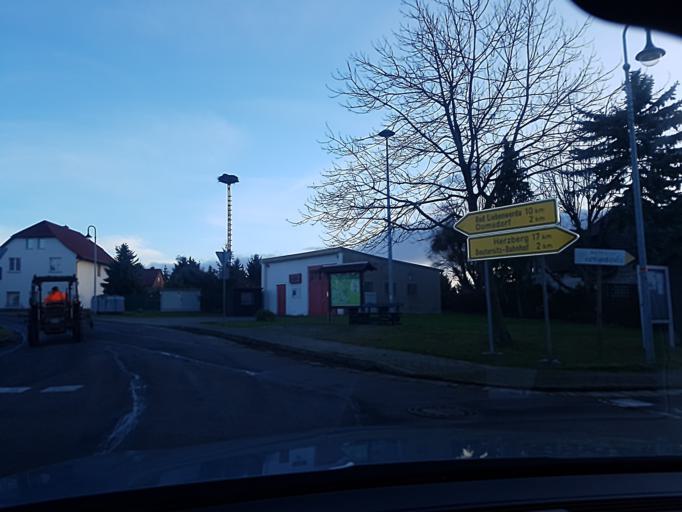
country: DE
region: Brandenburg
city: Schilda
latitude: 51.5870
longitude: 13.3844
